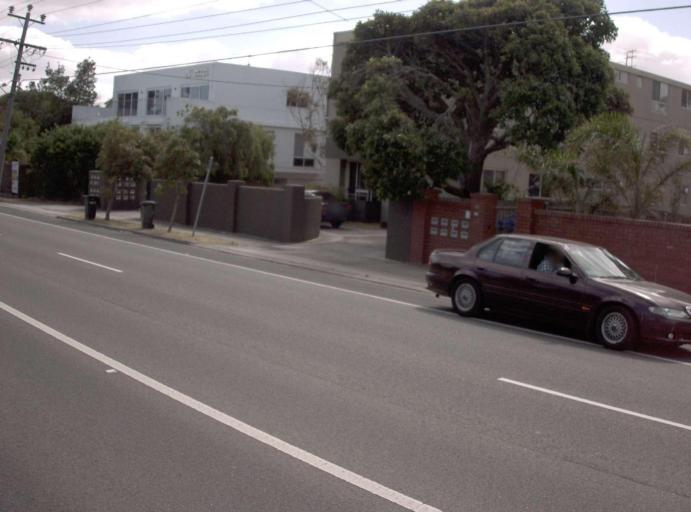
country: AU
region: Victoria
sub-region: Frankston
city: Frankston East
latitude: -38.1231
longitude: 145.1245
